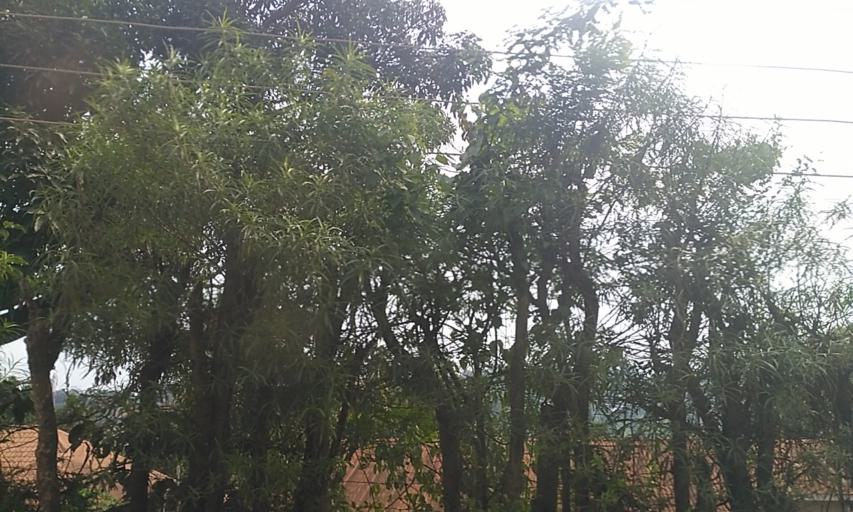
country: UG
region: Central Region
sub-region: Kampala District
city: Kampala
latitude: 0.3002
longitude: 32.5595
